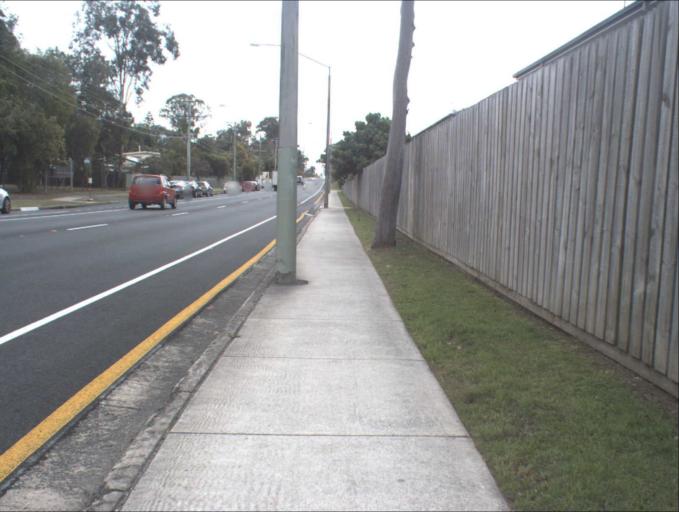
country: AU
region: Queensland
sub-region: Logan
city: Waterford West
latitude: -27.6705
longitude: 153.1351
